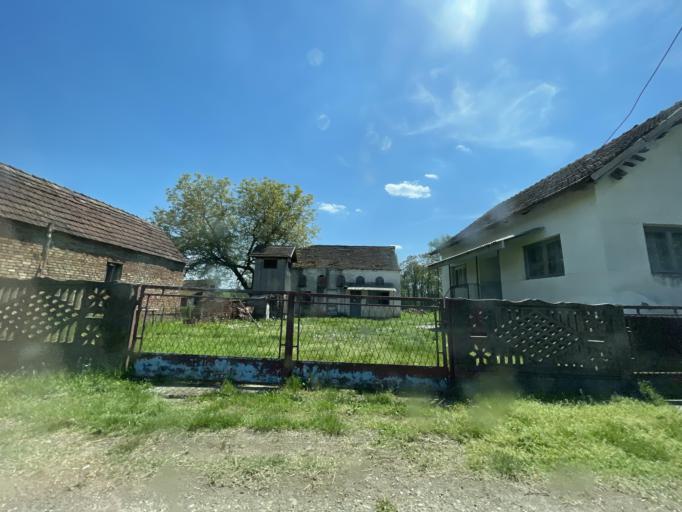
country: BA
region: Federation of Bosnia and Herzegovina
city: Donja Dubica
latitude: 45.0308
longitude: 18.4138
